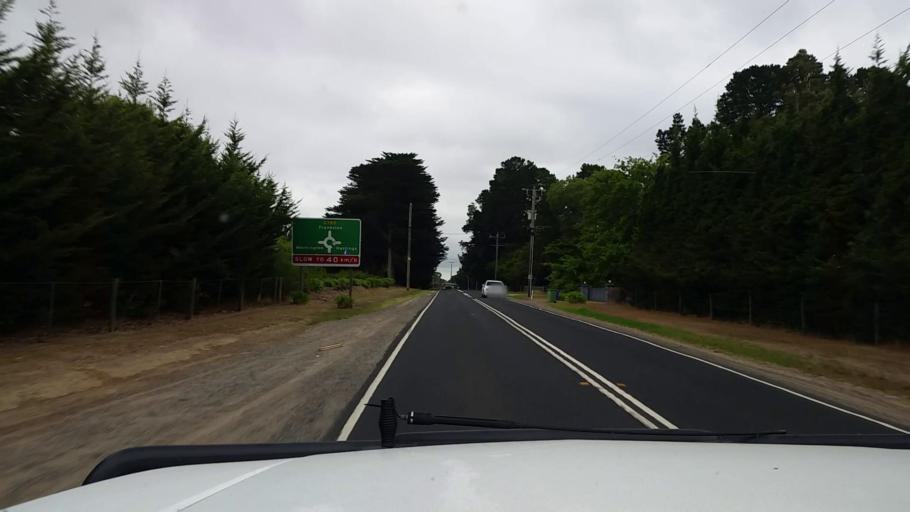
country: AU
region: Victoria
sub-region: Mornington Peninsula
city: Hastings
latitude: -38.2873
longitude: 145.1456
